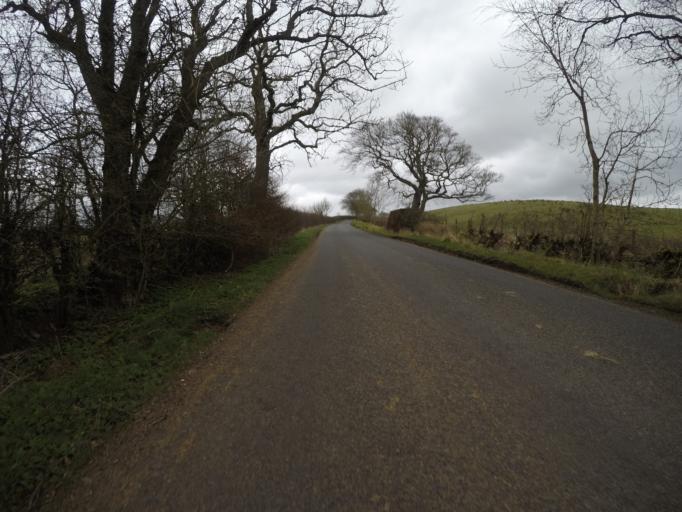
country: GB
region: Scotland
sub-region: East Ayrshire
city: Stewarton
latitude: 55.6802
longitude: -4.4483
